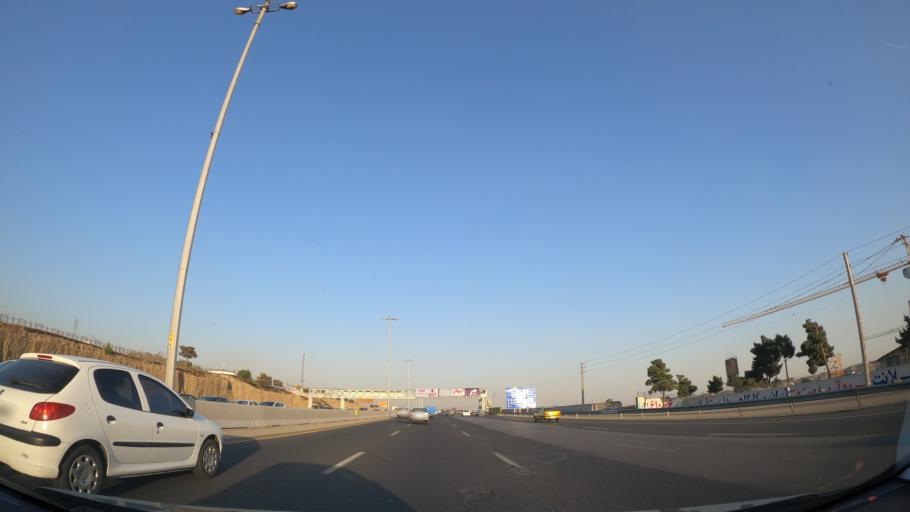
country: IR
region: Tehran
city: Shahr-e Qods
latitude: 35.7510
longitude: 51.0794
